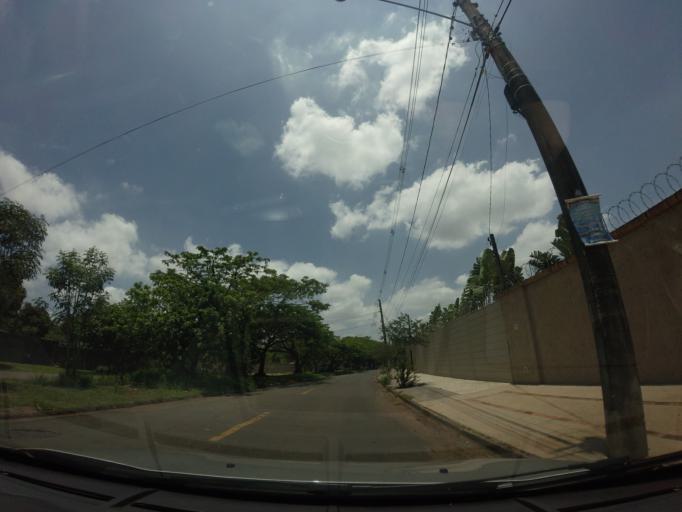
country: BR
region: Sao Paulo
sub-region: Piracicaba
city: Piracicaba
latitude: -22.7627
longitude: -47.5928
